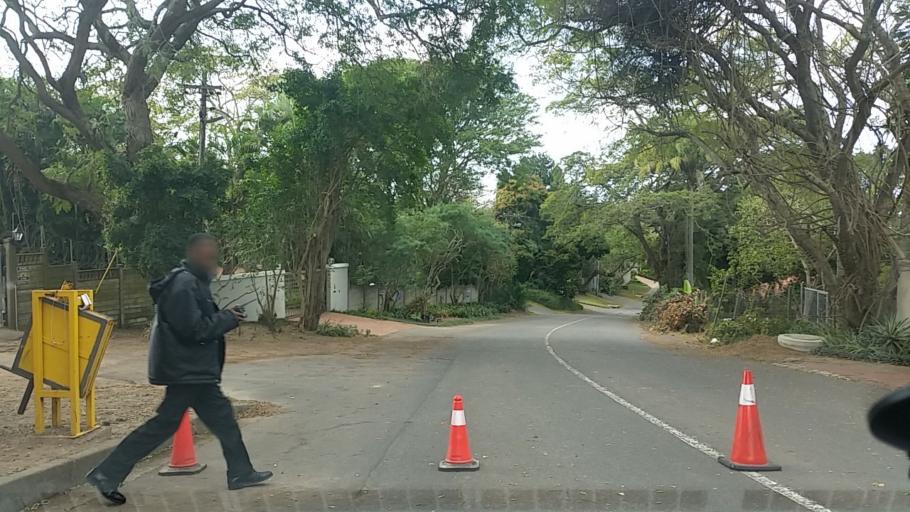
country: ZA
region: KwaZulu-Natal
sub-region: eThekwini Metropolitan Municipality
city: Berea
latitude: -29.8330
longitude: 30.9418
